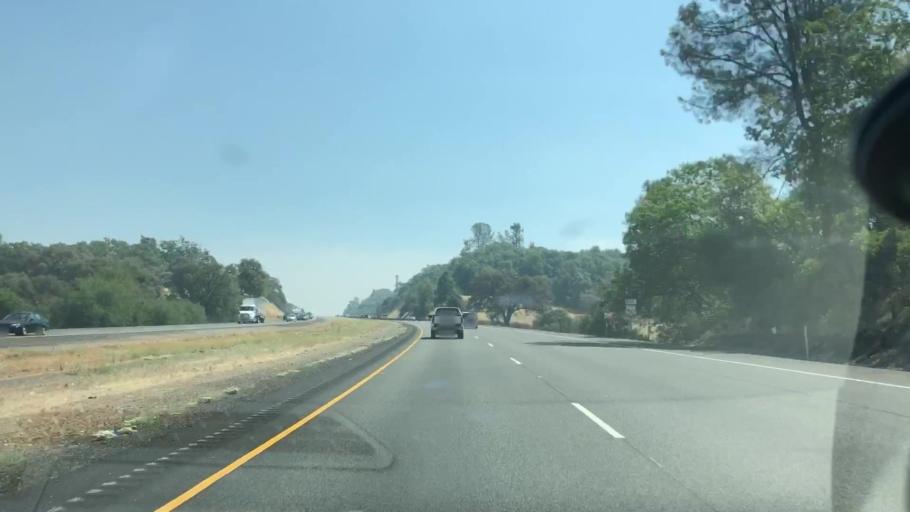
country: US
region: California
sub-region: El Dorado County
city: Shingle Springs
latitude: 38.6962
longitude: -120.8814
